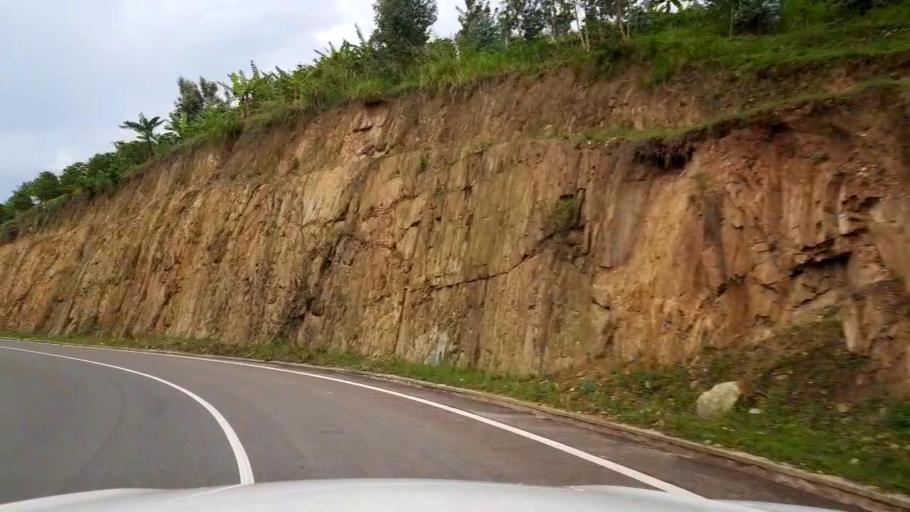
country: RW
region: Western Province
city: Kibuye
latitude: -2.0247
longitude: 29.3899
